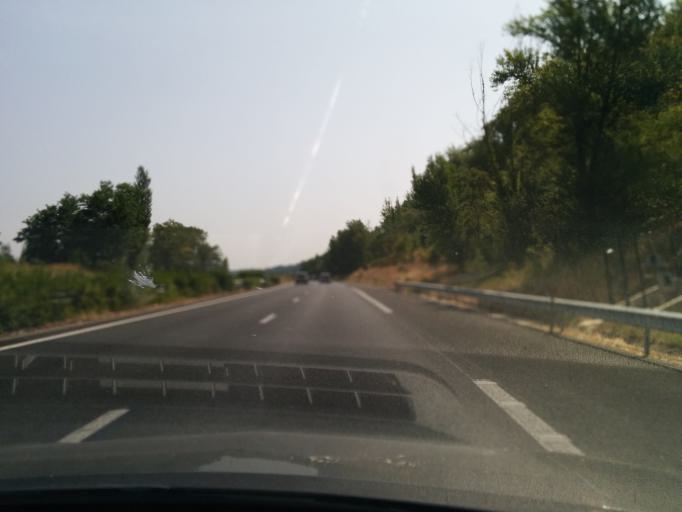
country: FR
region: Midi-Pyrenees
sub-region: Departement du Tarn
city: Lagrave
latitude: 43.8846
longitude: 2.0048
